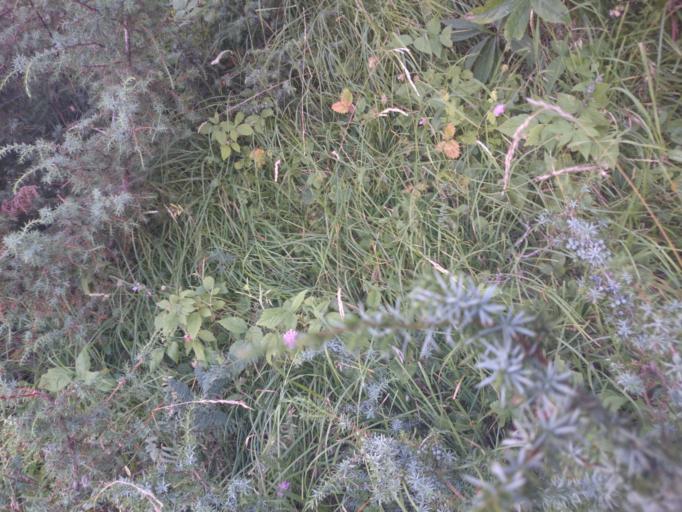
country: AL
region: Lezhe
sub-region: Rrethi i Mirdites
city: Orosh
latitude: 41.8610
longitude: 20.1171
